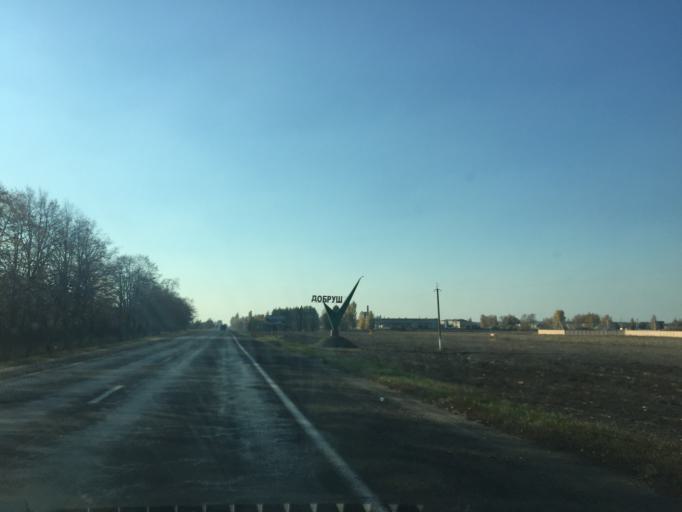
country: BY
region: Gomel
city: Dobrush
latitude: 52.3836
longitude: 31.3610
